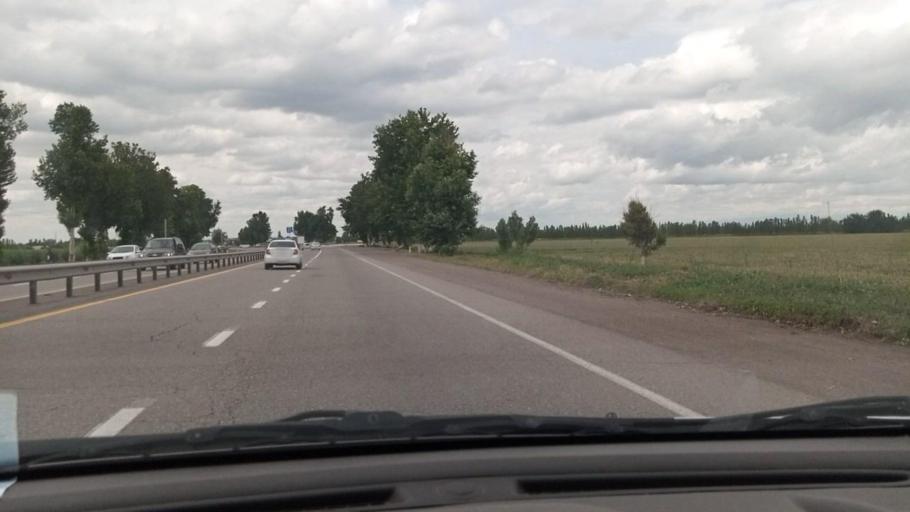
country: UZ
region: Toshkent Shahri
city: Bektemir
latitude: 41.1415
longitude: 69.4330
